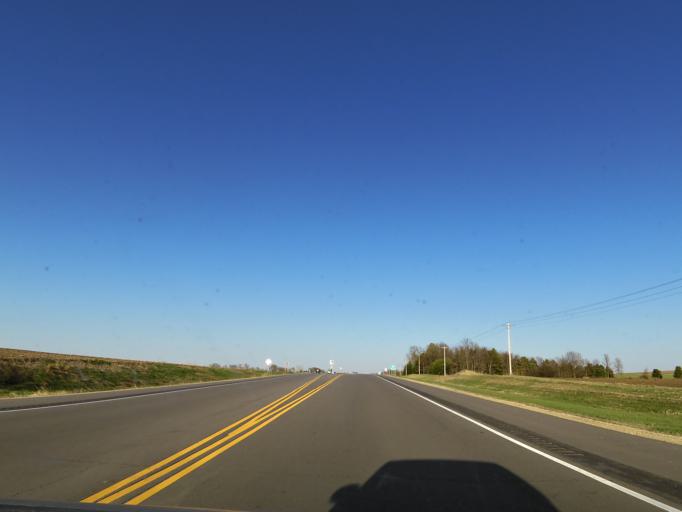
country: US
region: Wisconsin
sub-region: Pierce County
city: Prescott
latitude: 44.6007
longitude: -92.7846
